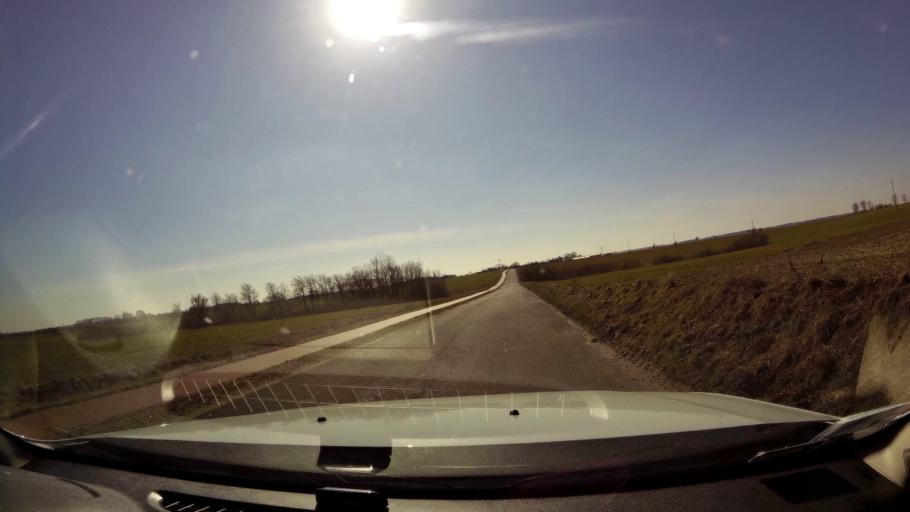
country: PL
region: West Pomeranian Voivodeship
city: Trzcinsko Zdroj
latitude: 52.9815
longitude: 14.6075
